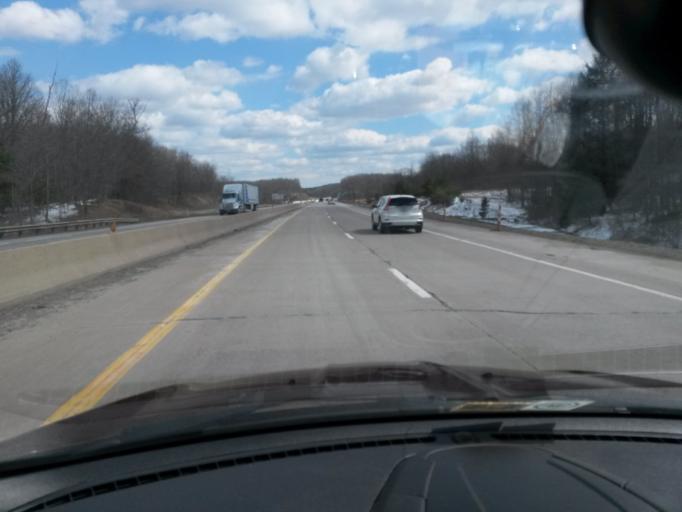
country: US
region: West Virginia
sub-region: Raleigh County
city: Daniels
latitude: 37.7714
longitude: -81.0461
